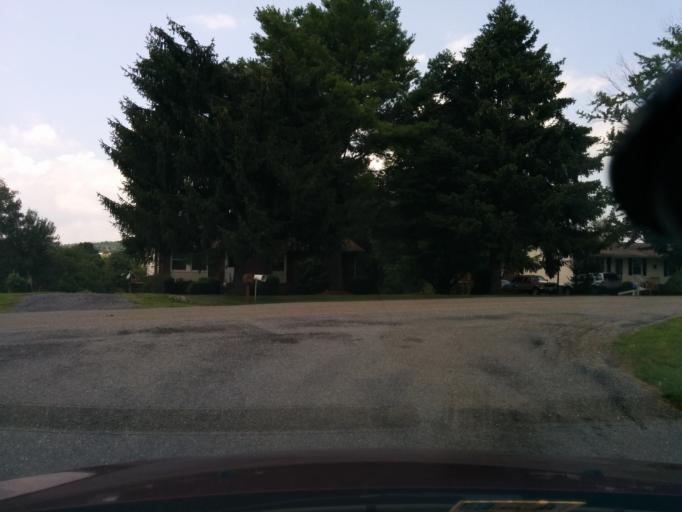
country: US
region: Virginia
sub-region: Rockbridge County
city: East Lexington
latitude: 37.8142
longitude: -79.4066
